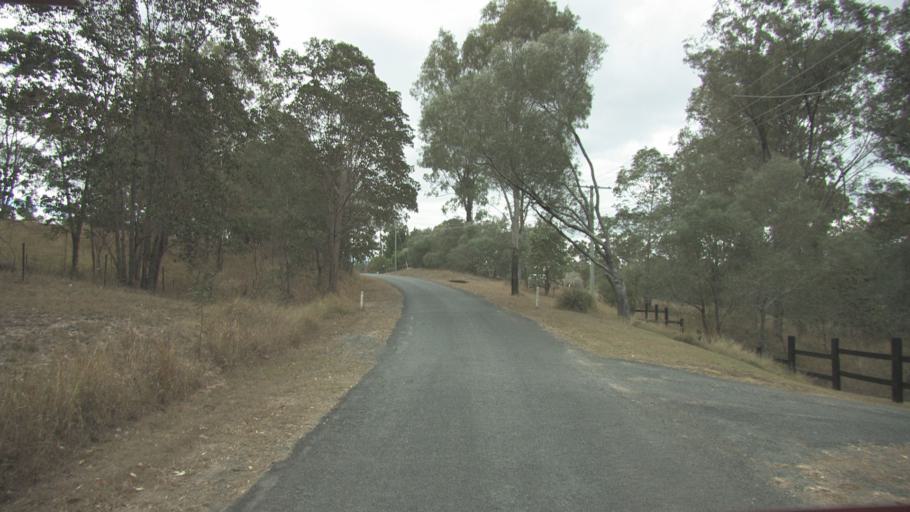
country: AU
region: Queensland
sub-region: Logan
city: Cedar Vale
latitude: -27.8864
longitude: 153.0345
